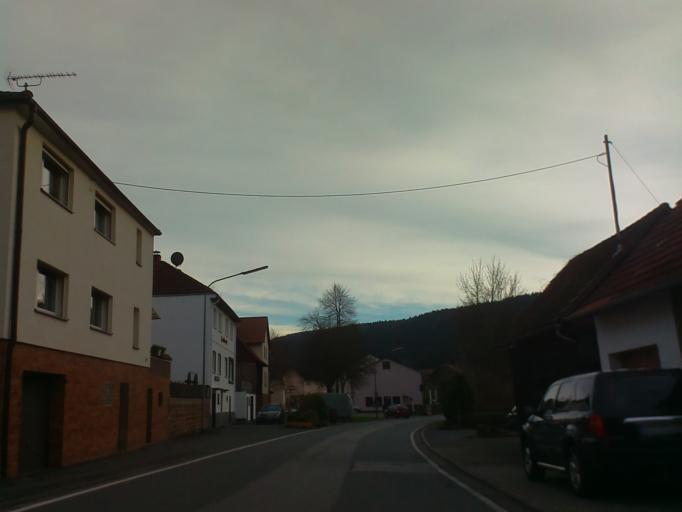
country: DE
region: Hesse
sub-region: Regierungsbezirk Darmstadt
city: Beerfelden
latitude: 49.6231
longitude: 8.9448
